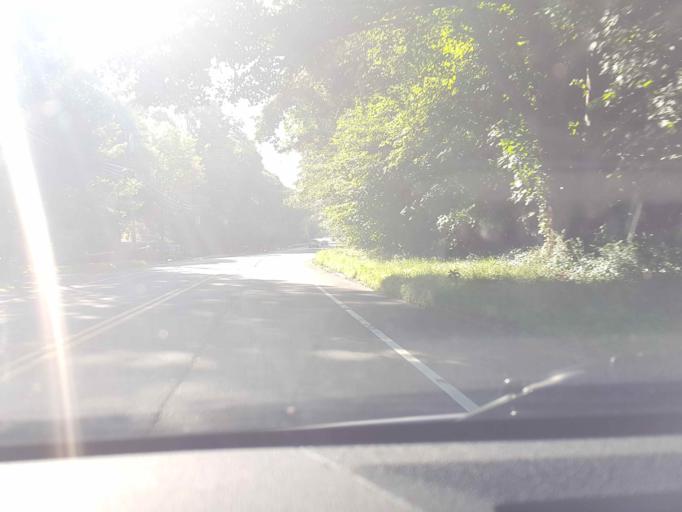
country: US
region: Connecticut
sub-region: New Haven County
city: Guilford
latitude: 41.3070
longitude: -72.7164
